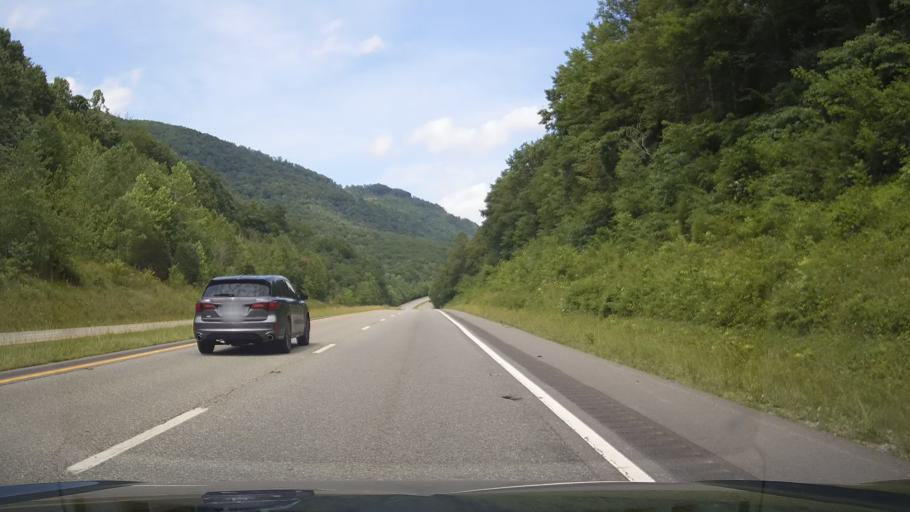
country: US
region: Virginia
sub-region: Wise County
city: Big Stone Gap
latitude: 36.8913
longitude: -82.7154
